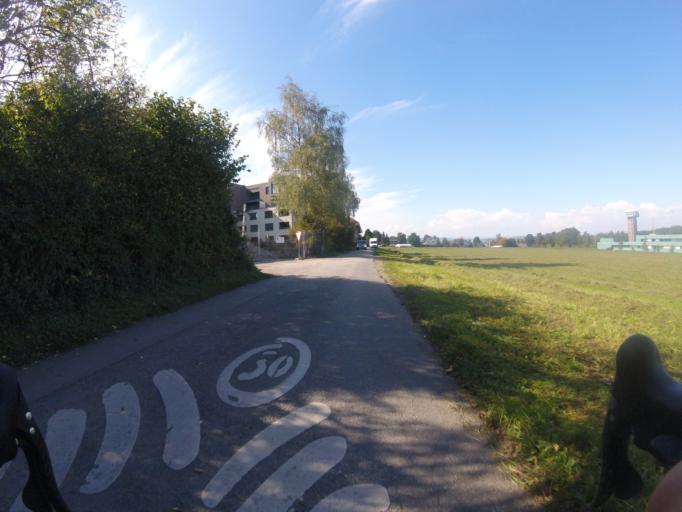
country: CH
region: Bern
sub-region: Bern-Mittelland District
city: Kehrsatz
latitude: 46.9218
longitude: 7.4642
